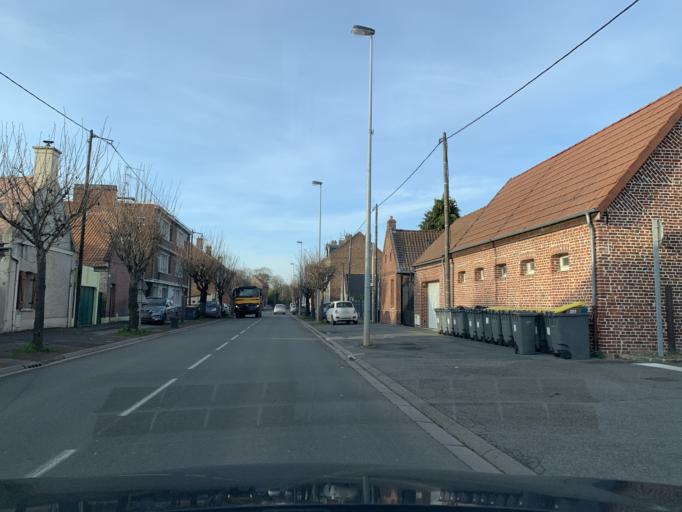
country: FR
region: Nord-Pas-de-Calais
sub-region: Departement du Nord
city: Cambrai
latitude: 50.1644
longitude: 3.2449
